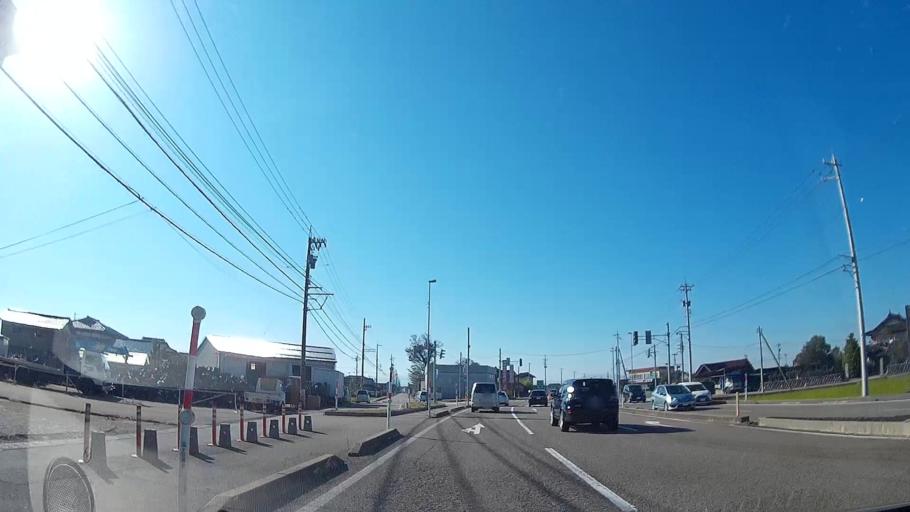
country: JP
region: Toyama
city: Takaoka
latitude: 36.6956
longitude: 136.9832
